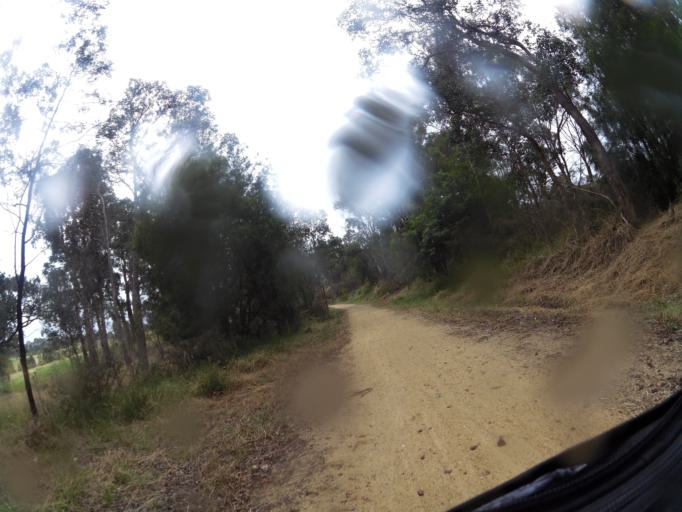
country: AU
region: Victoria
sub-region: East Gippsland
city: Lakes Entrance
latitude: -37.7597
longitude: 147.8169
